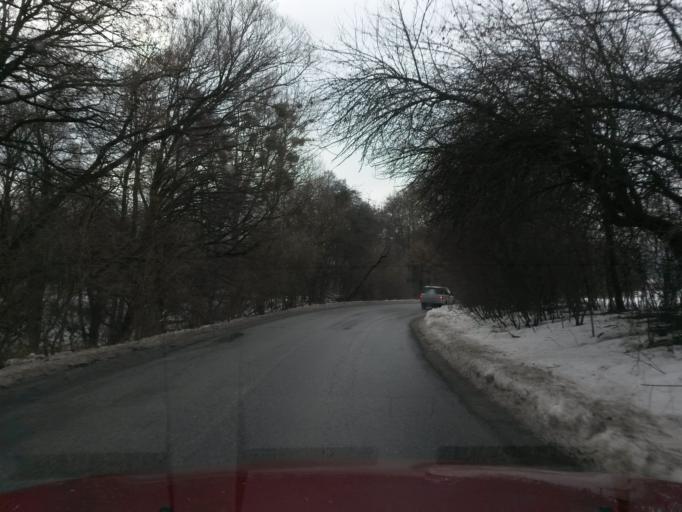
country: SK
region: Kosicky
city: Kosice
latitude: 48.7602
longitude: 21.3544
